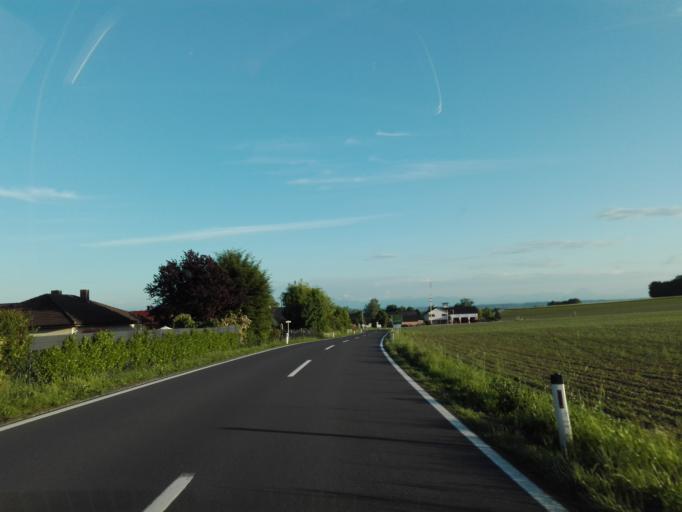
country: AT
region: Upper Austria
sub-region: Politischer Bezirk Linz-Land
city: Horsching
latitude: 48.2595
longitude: 14.1580
